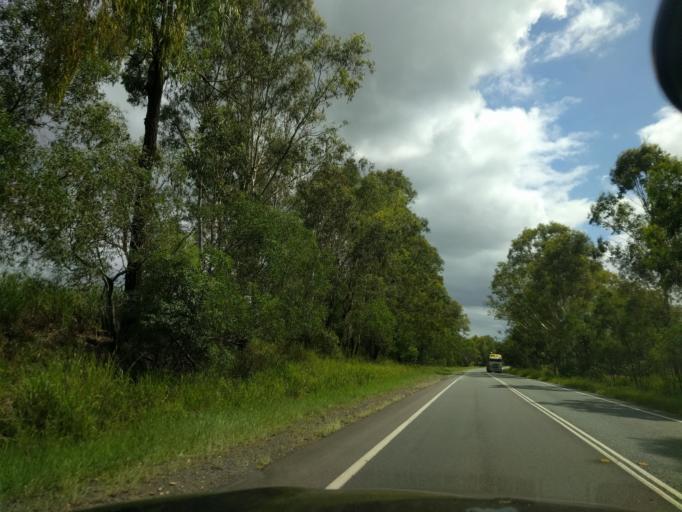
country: AU
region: Queensland
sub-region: Logan
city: Cedar Vale
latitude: -27.8614
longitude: 153.0015
